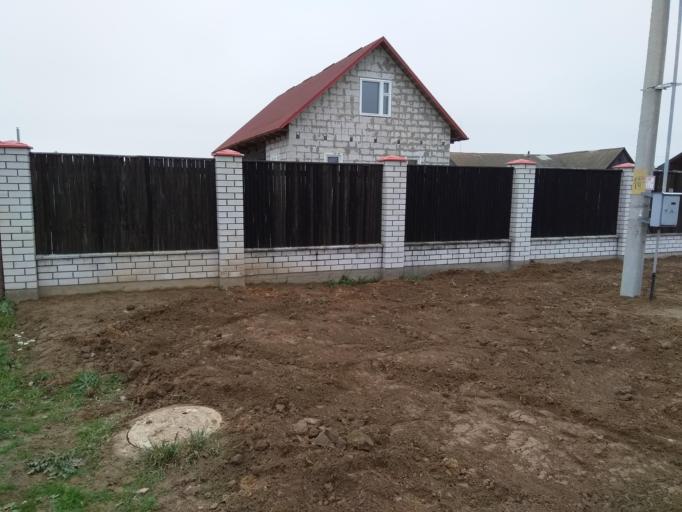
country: BY
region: Mogilev
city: Palykavichy Pyershyya
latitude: 53.9451
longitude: 30.3913
